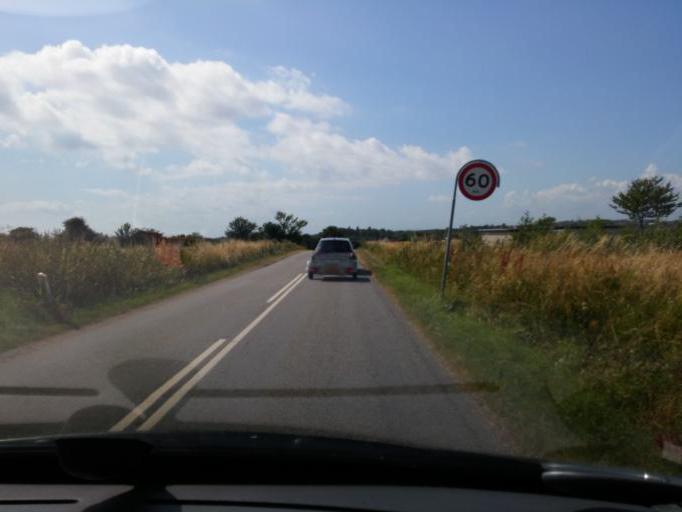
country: DK
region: South Denmark
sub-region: Langeland Kommune
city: Rudkobing
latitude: 54.8175
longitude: 10.6637
